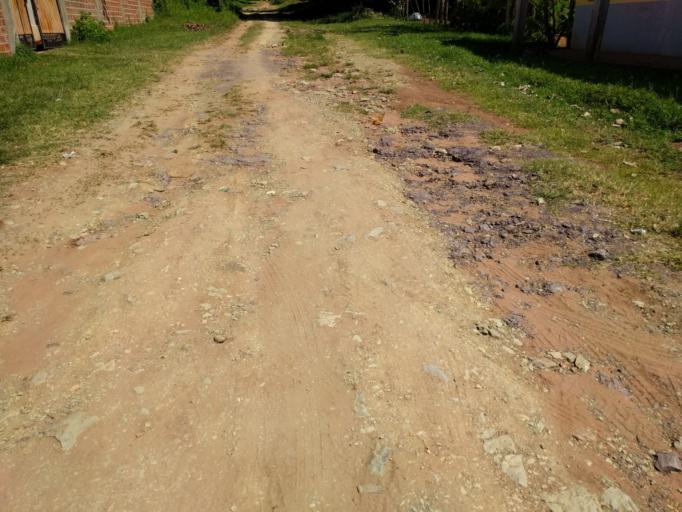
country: BO
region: Santa Cruz
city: Robore
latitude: -18.3390
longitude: -59.5961
